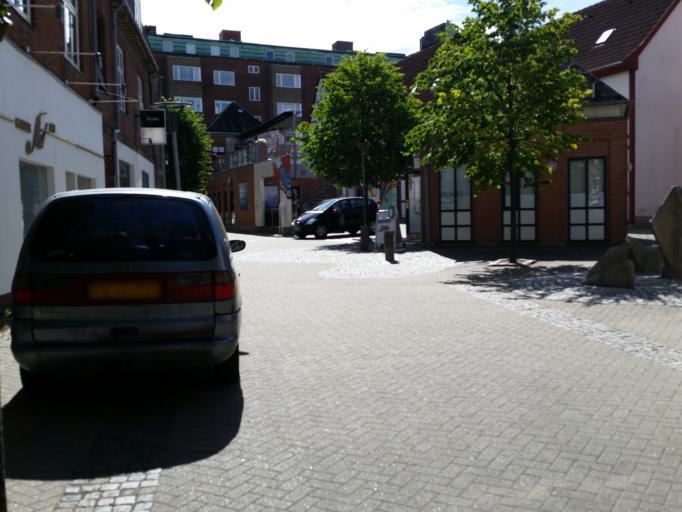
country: DK
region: North Denmark
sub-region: Alborg Kommune
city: Aalborg
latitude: 57.0492
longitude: 9.9151
